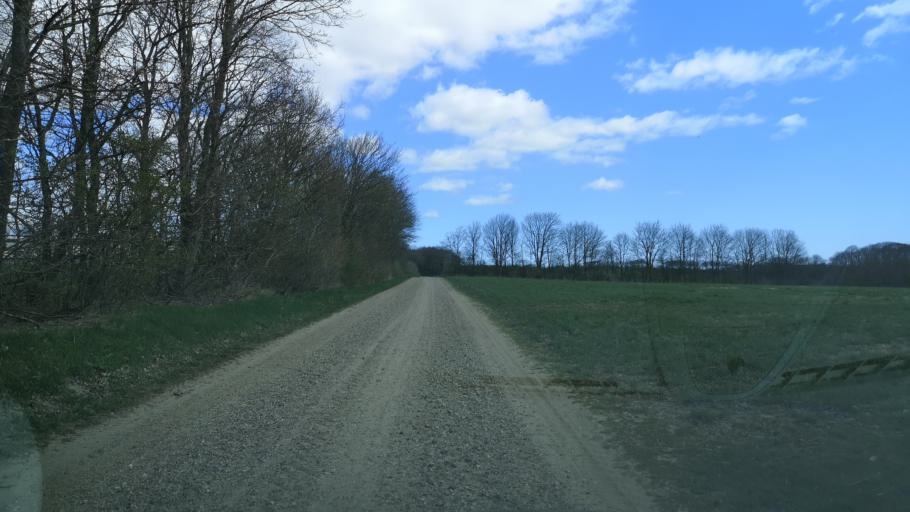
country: DK
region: Central Jutland
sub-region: Ringkobing-Skjern Kommune
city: Skjern
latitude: 55.9727
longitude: 8.5029
